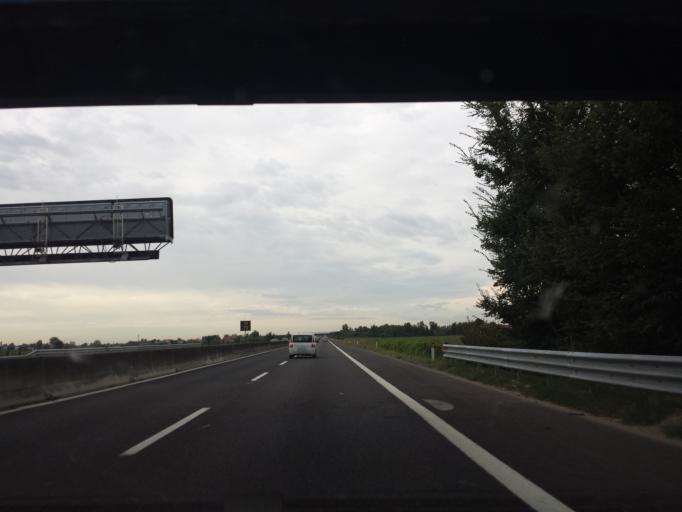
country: IT
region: Veneto
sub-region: Provincia di Padova
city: Monselice
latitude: 45.2211
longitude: 11.7746
